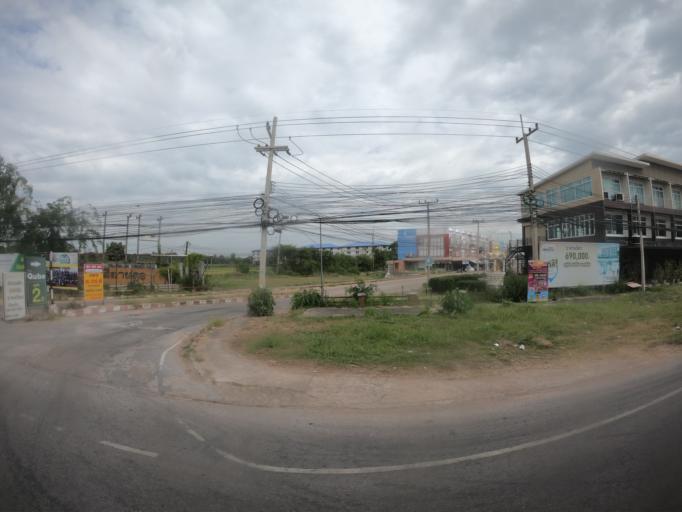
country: TH
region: Maha Sarakham
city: Maha Sarakham
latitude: 16.2102
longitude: 103.2831
